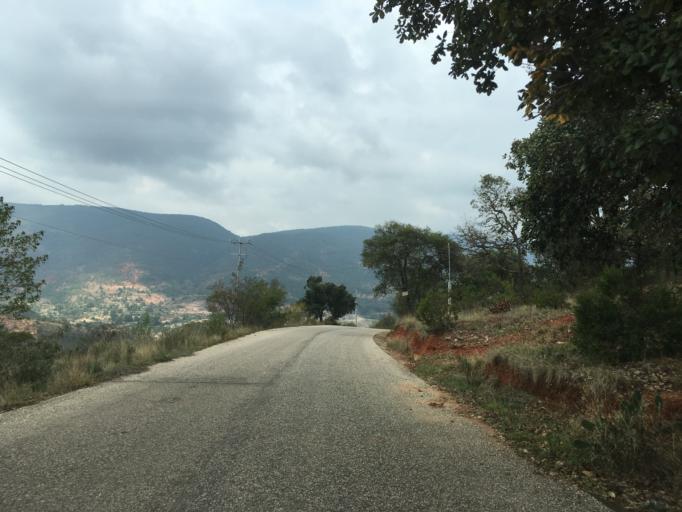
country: MX
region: Oaxaca
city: Santiago Tilantongo
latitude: 17.2578
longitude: -97.2974
